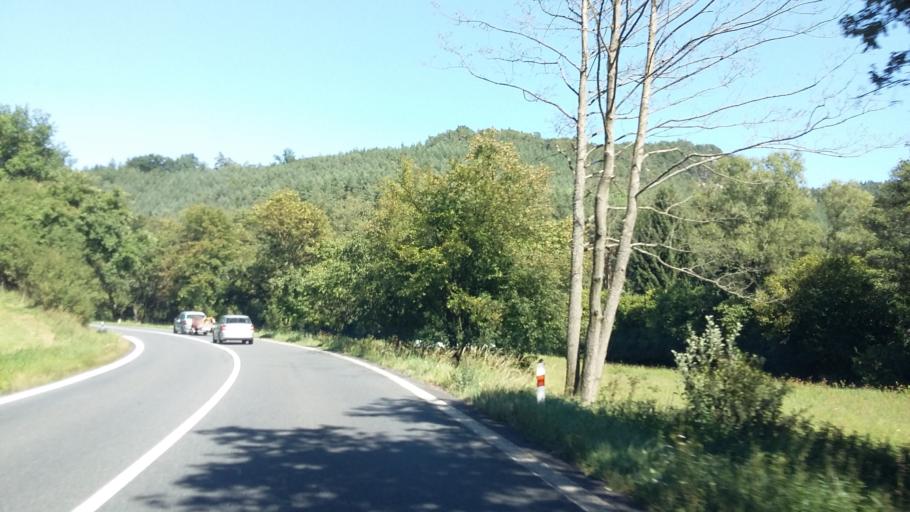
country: CZ
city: Duba
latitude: 50.5107
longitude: 14.4920
